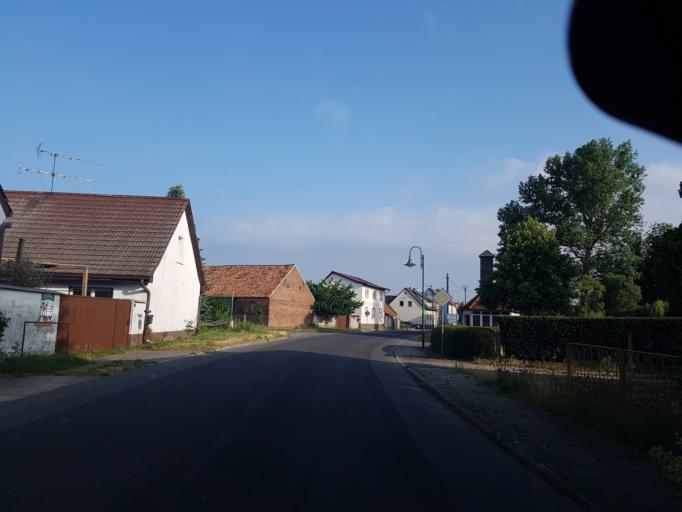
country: DE
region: Saxony-Anhalt
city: Holzdorf
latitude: 51.8410
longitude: 13.1627
